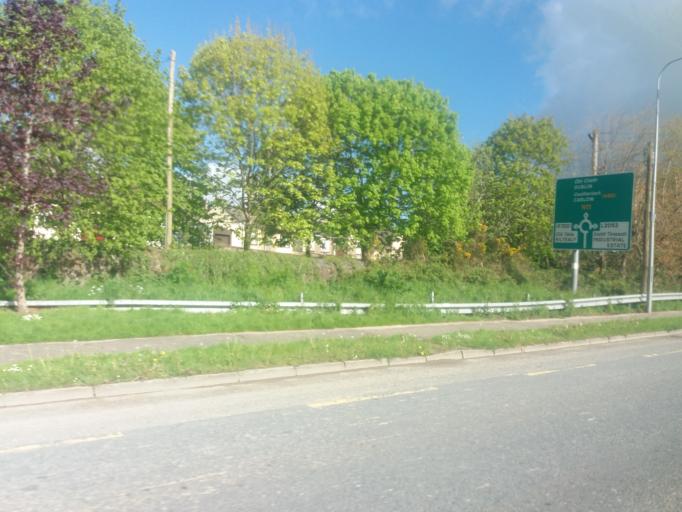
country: IE
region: Leinster
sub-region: Loch Garman
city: Enniscorthy
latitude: 52.5112
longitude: -6.5645
